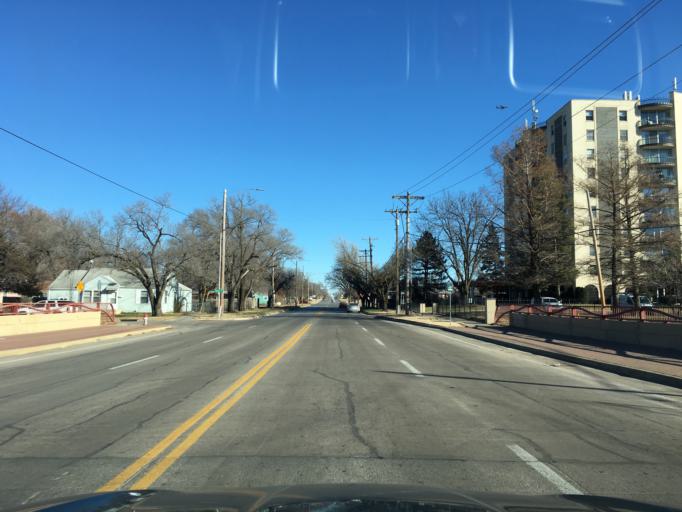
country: US
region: Kansas
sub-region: Sedgwick County
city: Wichita
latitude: 37.6719
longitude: -97.2788
